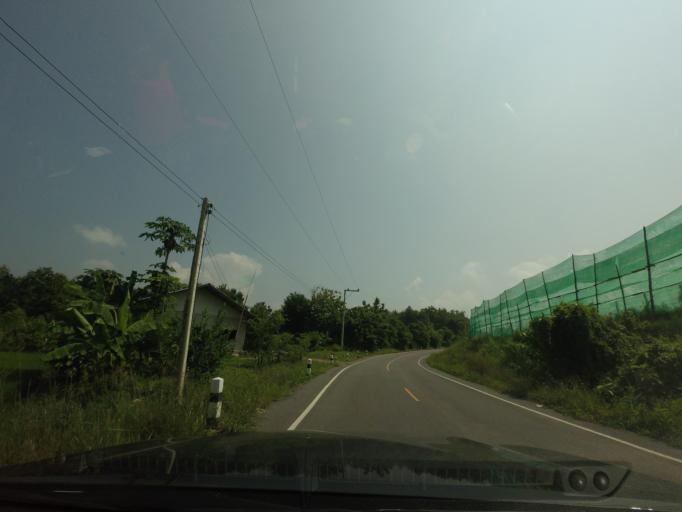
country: TH
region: Nan
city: Nan
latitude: 18.8562
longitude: 100.8010
